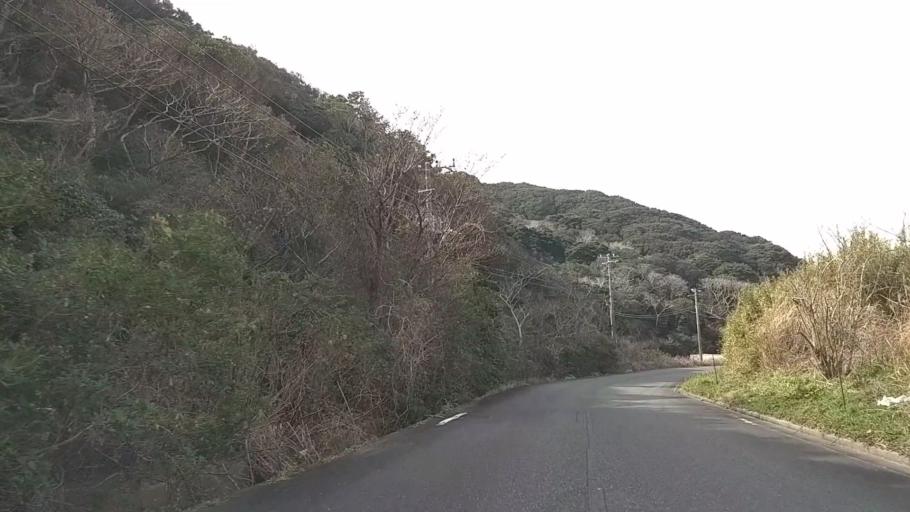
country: JP
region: Shizuoka
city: Shimoda
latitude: 34.6662
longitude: 138.9619
